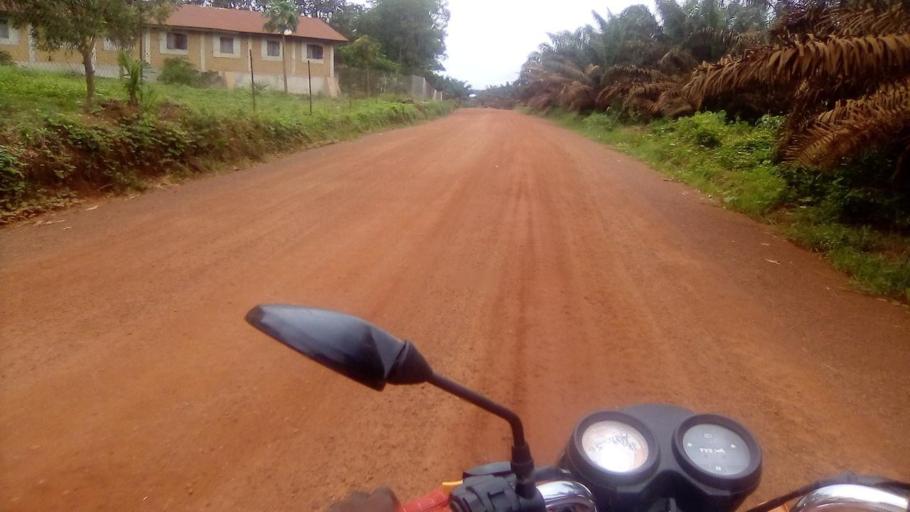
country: SL
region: Southern Province
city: Tongole
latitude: 7.4345
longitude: -11.8590
